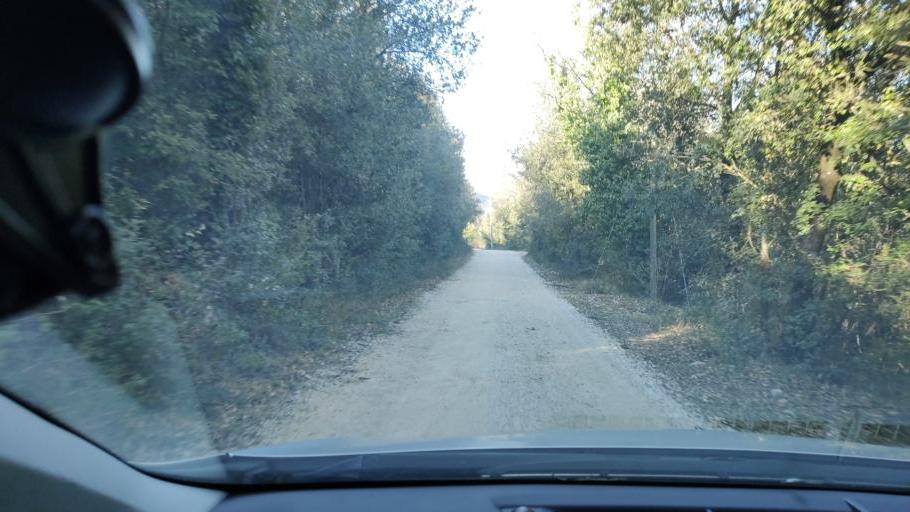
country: IT
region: Umbria
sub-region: Provincia di Terni
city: Amelia
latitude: 42.5618
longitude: 12.4414
